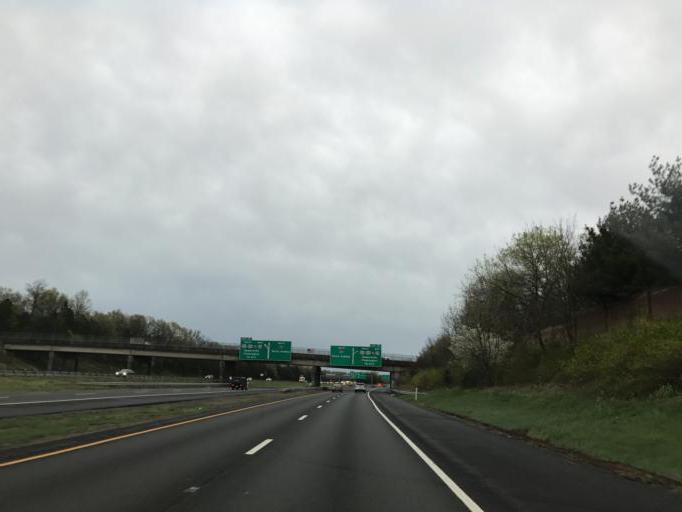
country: US
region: New Jersey
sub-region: Somerset County
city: Bridgewater
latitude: 40.6106
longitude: -74.6313
